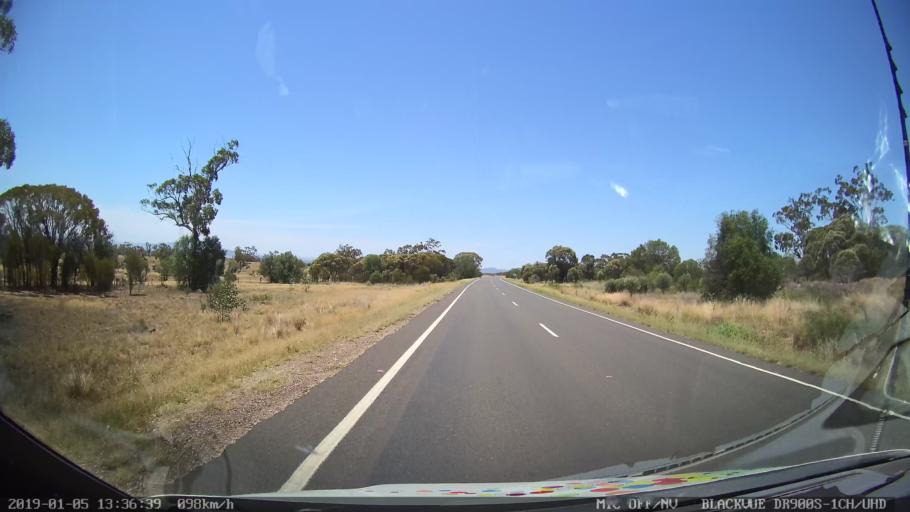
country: AU
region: New South Wales
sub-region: Gunnedah
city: Gunnedah
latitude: -30.9837
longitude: 150.1681
